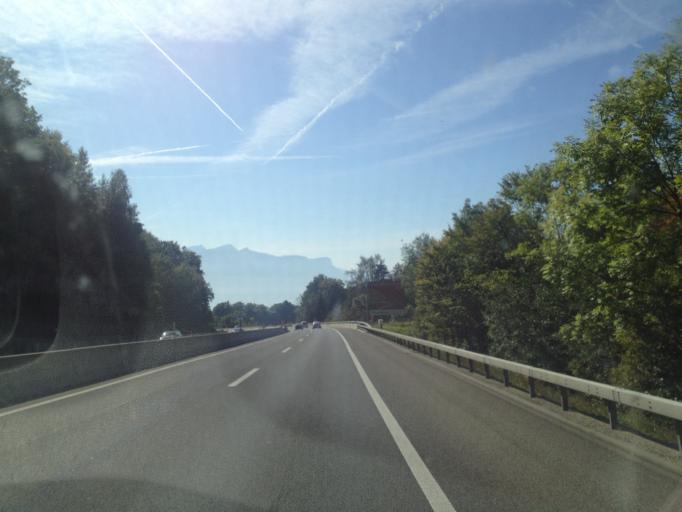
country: CH
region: Fribourg
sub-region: Veveyse District
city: Chatel-Saint-Denis
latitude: 46.5025
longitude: 6.8977
